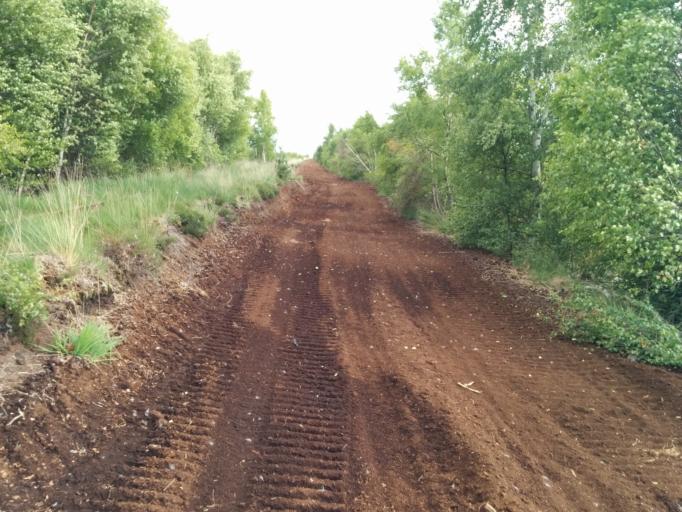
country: DE
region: Lower Saxony
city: Lohne
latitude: 52.6462
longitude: 8.2951
